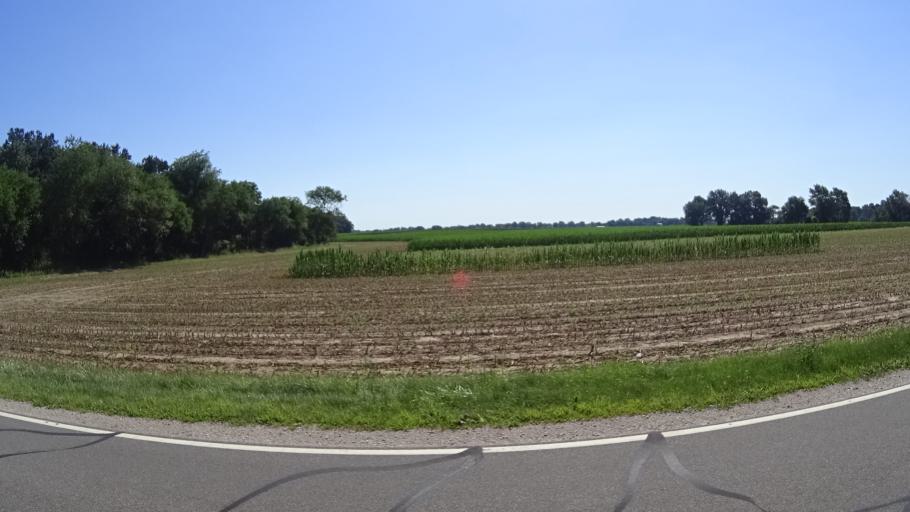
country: US
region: Ohio
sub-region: Erie County
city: Huron
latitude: 41.3814
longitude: -82.5905
